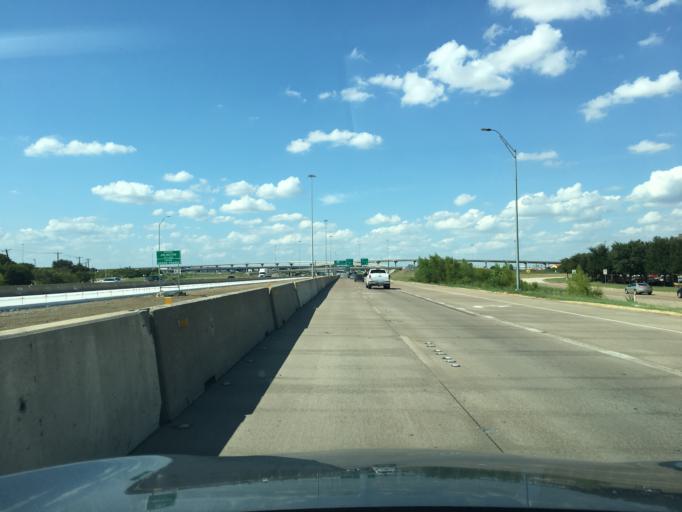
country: US
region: Texas
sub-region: Tarrant County
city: Arlington
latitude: 32.6688
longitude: -97.0626
